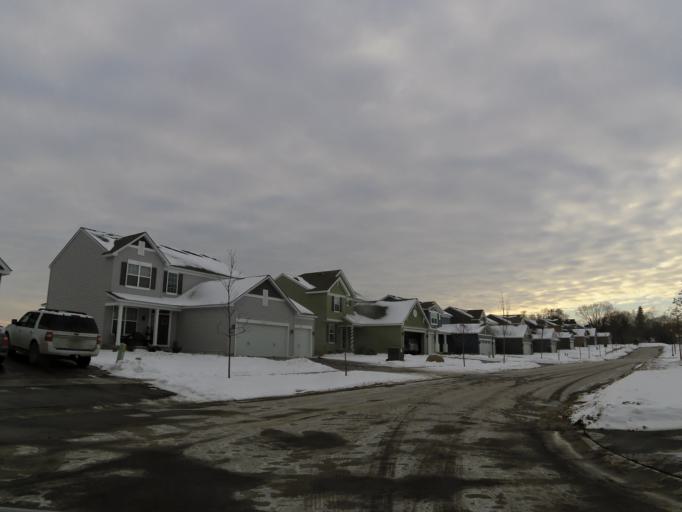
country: US
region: Minnesota
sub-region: Washington County
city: Lake Elmo
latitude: 44.9531
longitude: -92.8791
